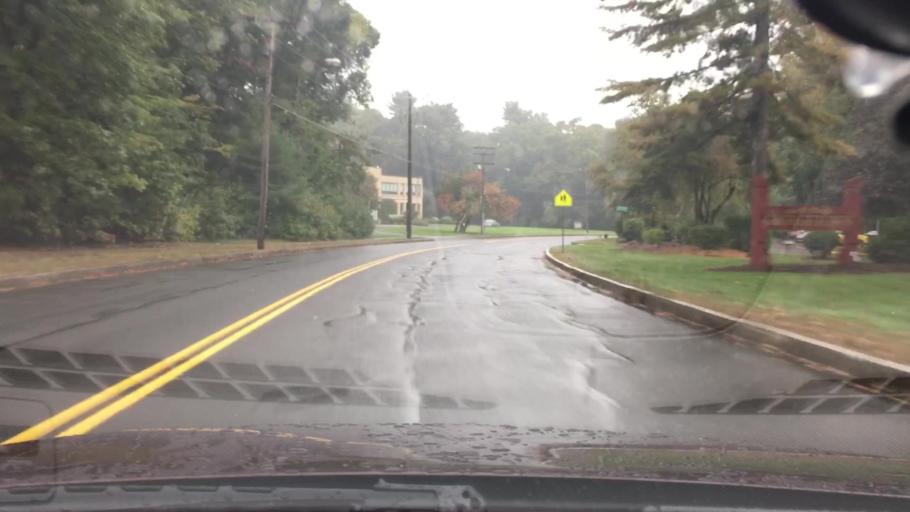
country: US
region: Massachusetts
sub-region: Hampden County
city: Longmeadow
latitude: 42.0687
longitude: -72.5553
